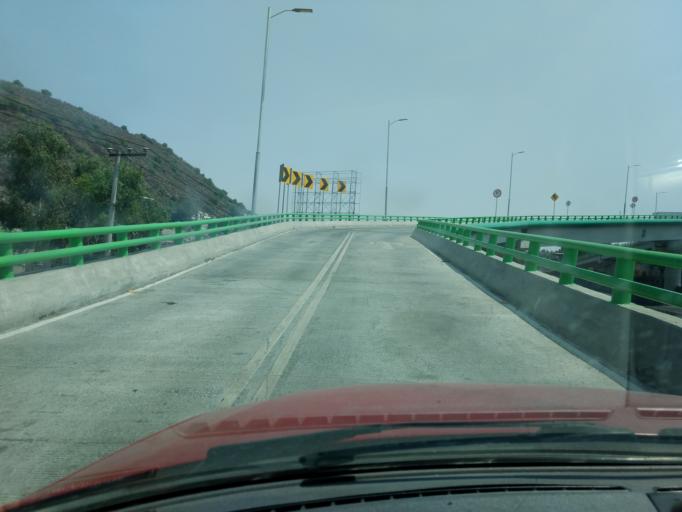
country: MX
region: Mexico
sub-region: La Paz
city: Emiliano Zapata
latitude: 19.3419
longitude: -98.9773
